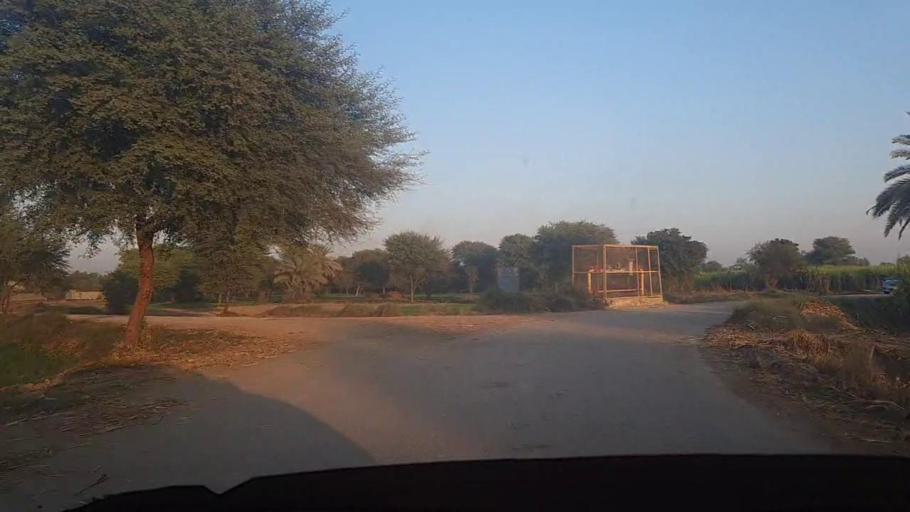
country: PK
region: Sindh
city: Sobhadero
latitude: 27.3521
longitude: 68.3736
